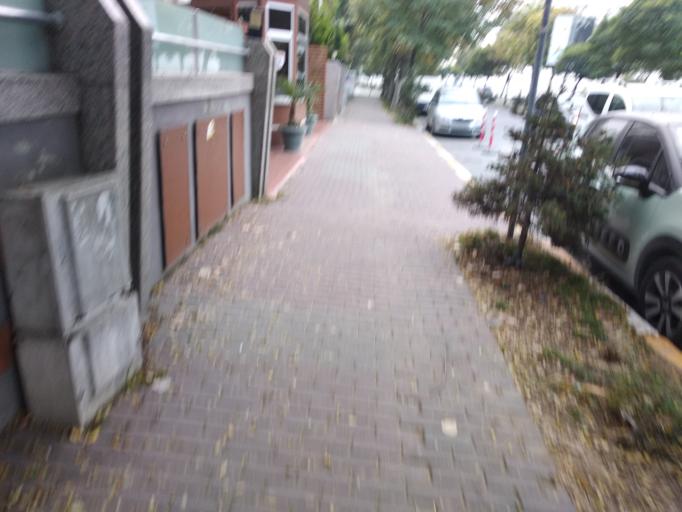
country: TR
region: Istanbul
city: Beylikduezue
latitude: 41.0032
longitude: 28.6385
